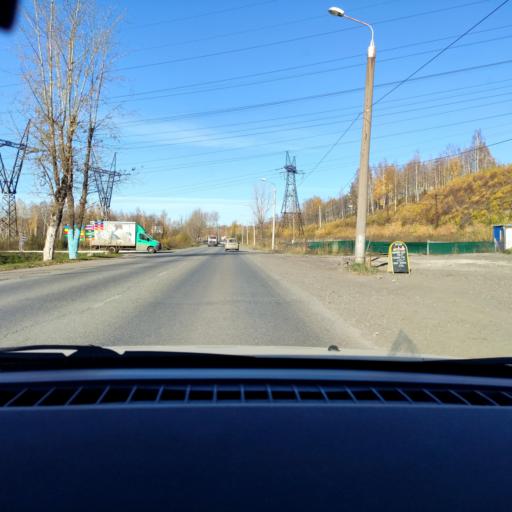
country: RU
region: Perm
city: Perm
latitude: 58.1075
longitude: 56.3624
